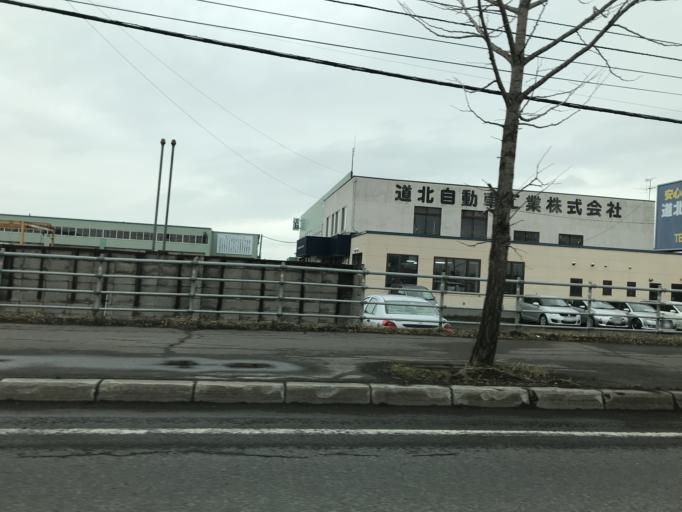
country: JP
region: Hokkaido
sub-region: Asahikawa-shi
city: Asahikawa
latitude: 43.8177
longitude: 142.4061
